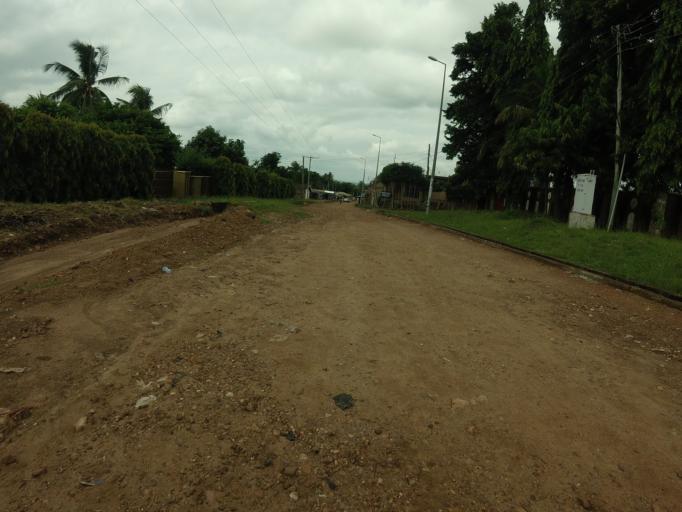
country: GH
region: Volta
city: Ho
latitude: 6.5945
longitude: 0.4697
